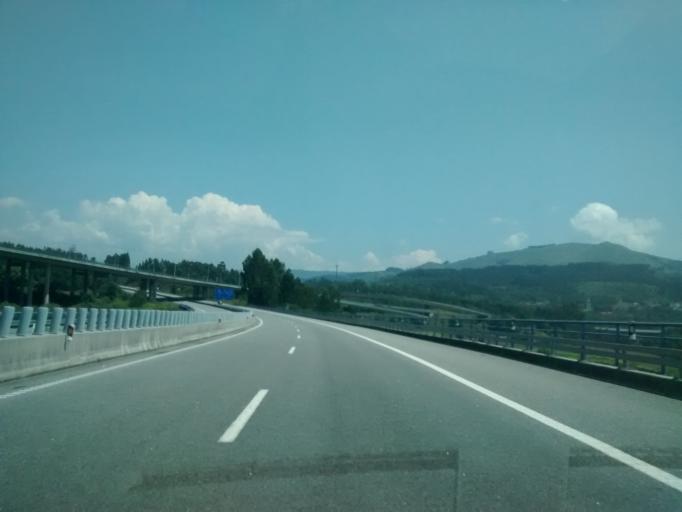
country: PT
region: Viana do Castelo
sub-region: Ponte de Lima
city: Ponte de Lima
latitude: 41.7791
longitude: -8.5672
